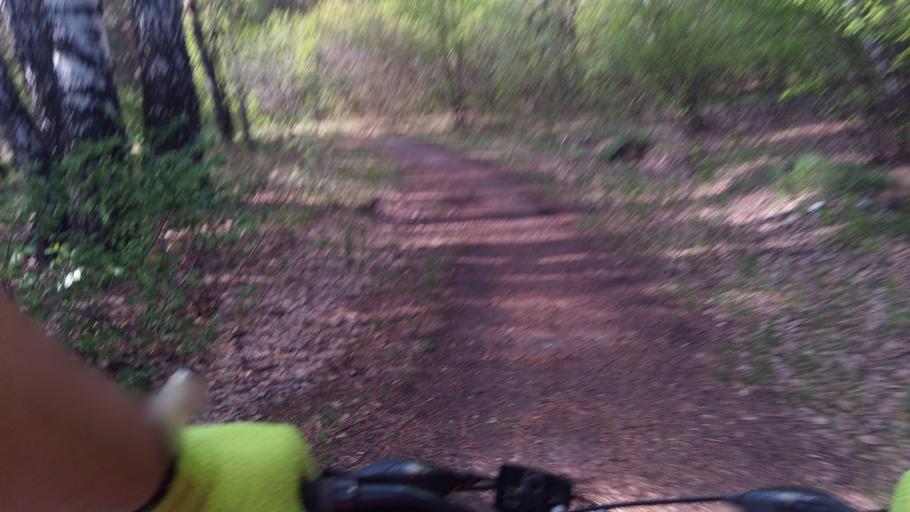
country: RU
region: Chelyabinsk
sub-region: Gorod Chelyabinsk
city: Chelyabinsk
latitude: 55.1614
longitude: 61.3168
